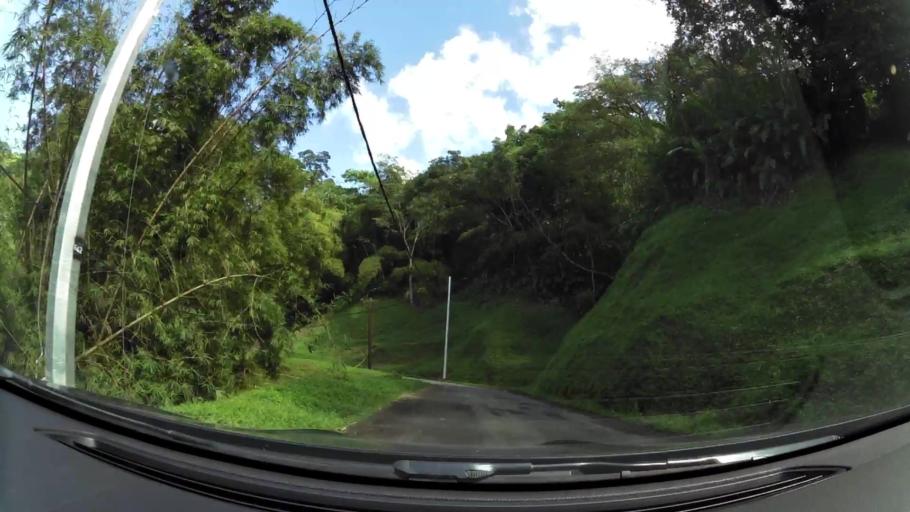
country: TT
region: Eastern Tobago
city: Roxborough
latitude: 11.3031
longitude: -60.6259
